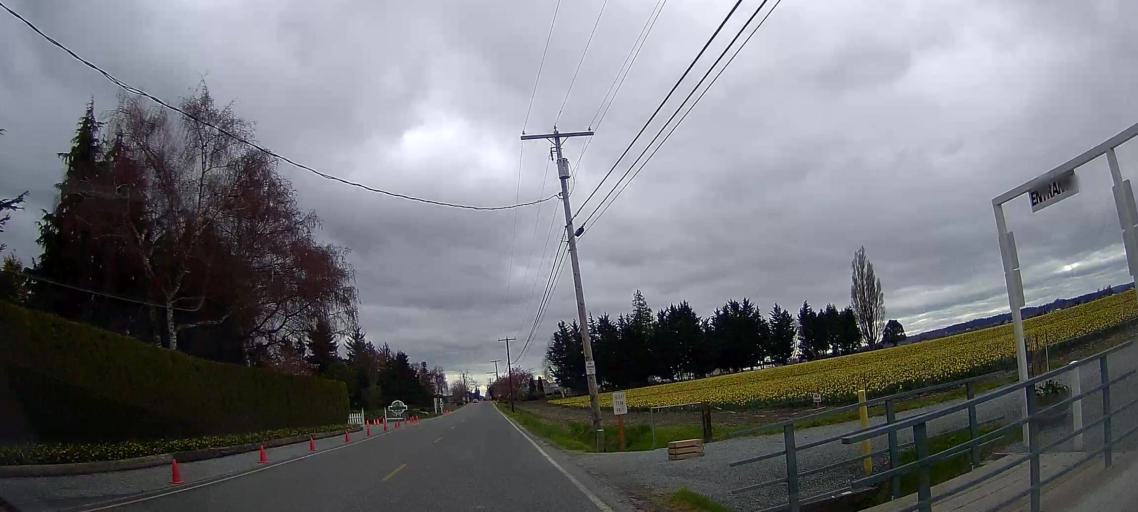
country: US
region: Washington
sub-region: Skagit County
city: Mount Vernon
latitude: 48.4160
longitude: -122.4010
